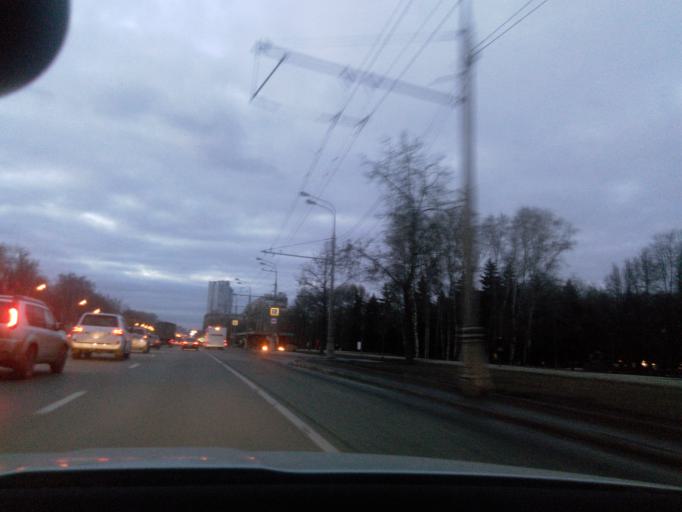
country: RU
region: Moskovskaya
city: Levoberezhnyy
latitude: 55.8513
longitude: 37.4732
